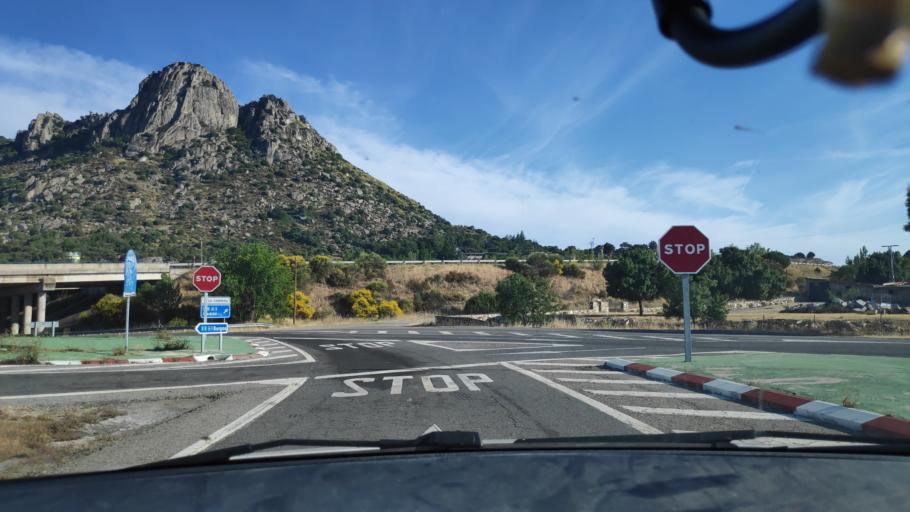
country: ES
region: Madrid
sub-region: Provincia de Madrid
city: La Cabrera
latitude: 40.8736
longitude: -3.6004
